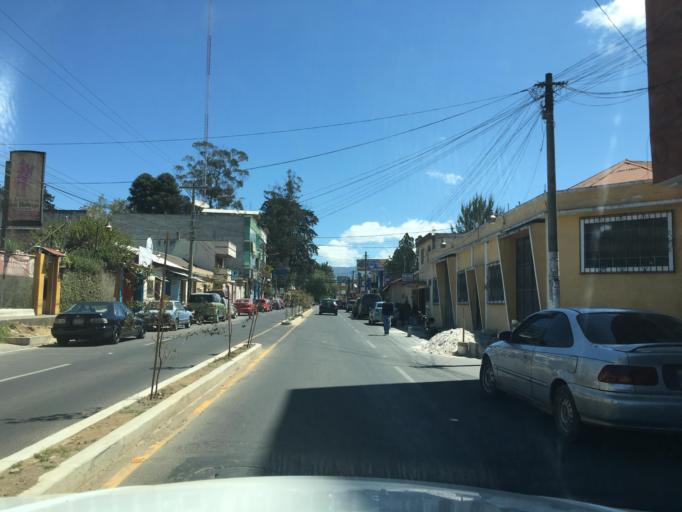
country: GT
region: Quetzaltenango
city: Quetzaltenango
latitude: 14.8448
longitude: -91.5182
